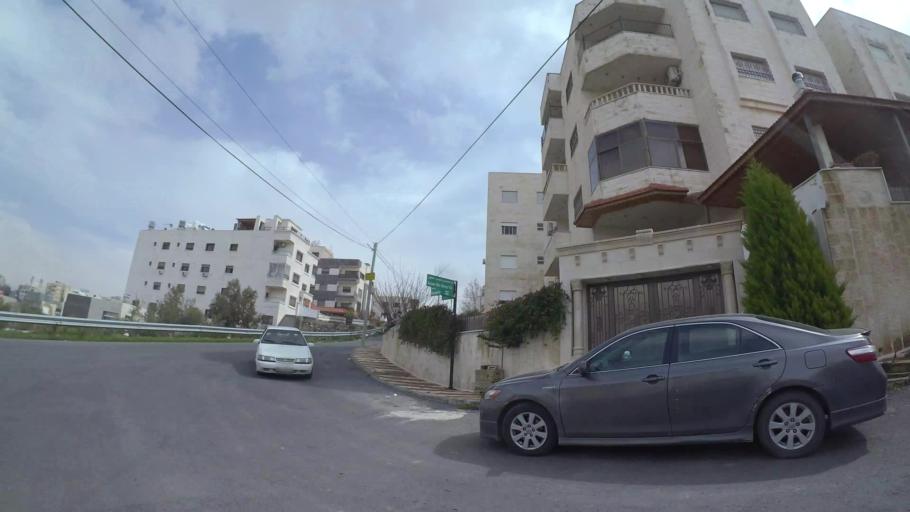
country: JO
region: Amman
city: Umm as Summaq
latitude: 31.8984
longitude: 35.8357
